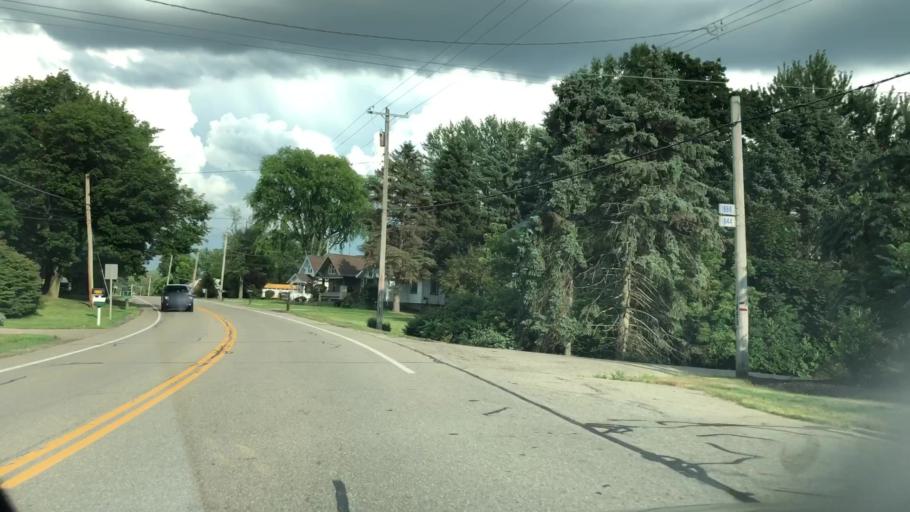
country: US
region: Ohio
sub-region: Summit County
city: Green
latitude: 40.9332
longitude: -81.4790
